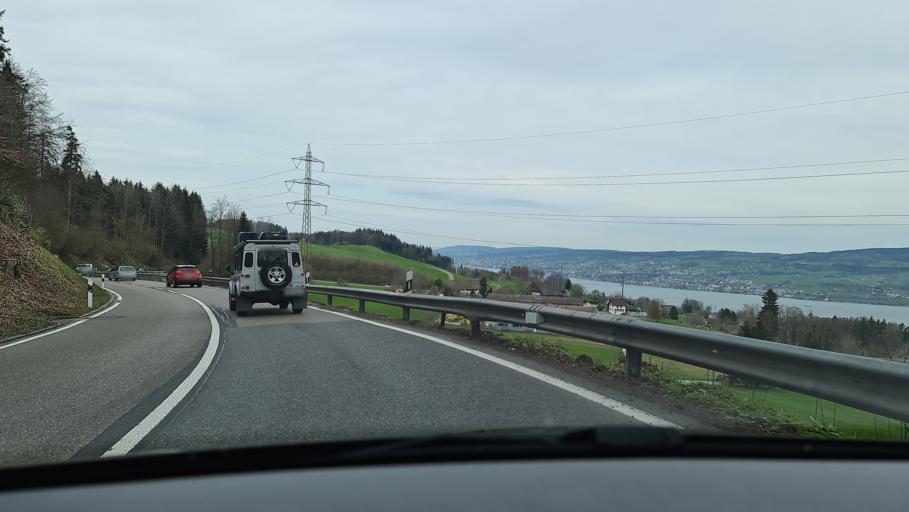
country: CH
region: Zurich
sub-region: Bezirk Horgen
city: Horgen / Allmend
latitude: 47.2274
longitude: 8.6125
